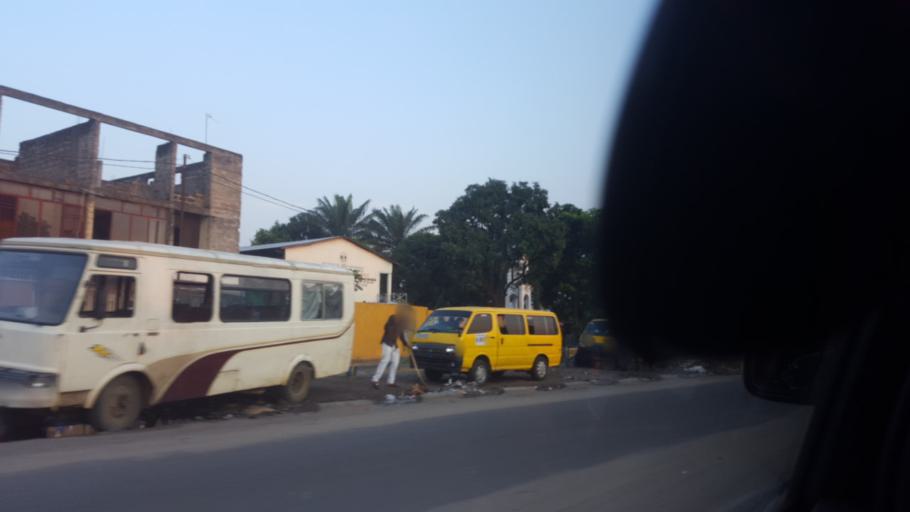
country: CD
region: Kinshasa
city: Kinshasa
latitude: -4.3458
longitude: 15.3250
